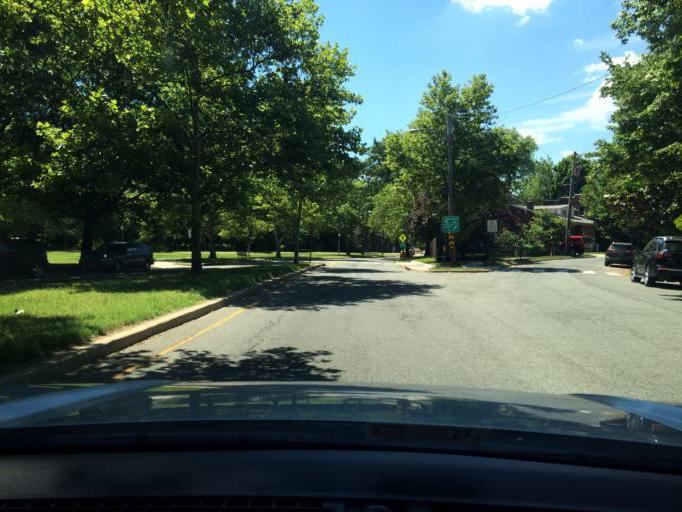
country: US
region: Virginia
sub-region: City of Alexandria
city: Alexandria
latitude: 38.8089
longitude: -77.0606
